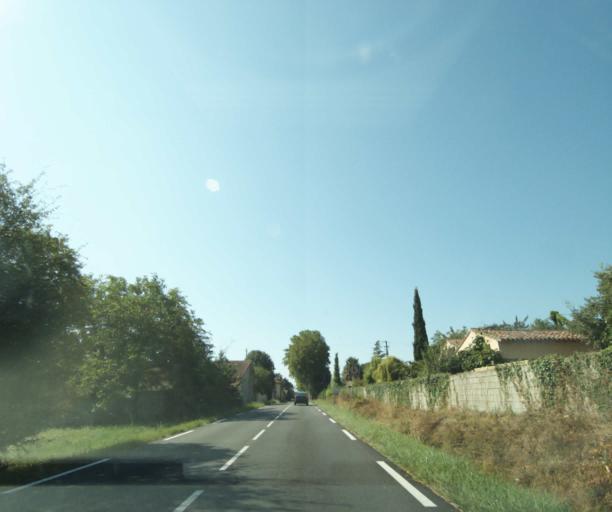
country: FR
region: Midi-Pyrenees
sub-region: Departement de la Haute-Garonne
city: Saint-Sulpice-sur-Leze
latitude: 43.3339
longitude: 1.3219
